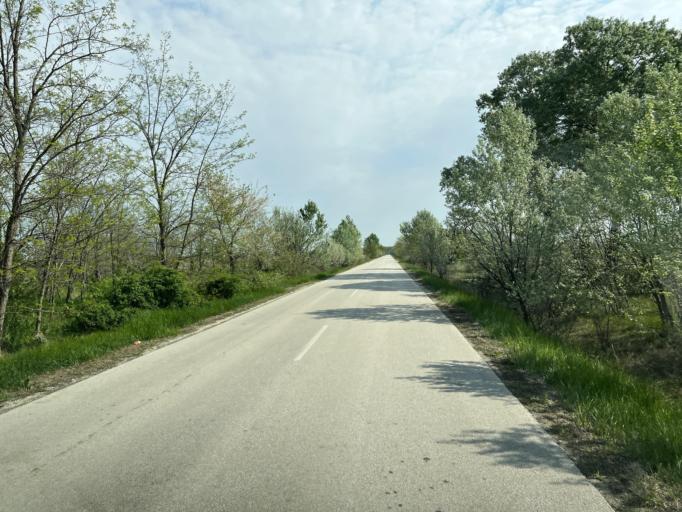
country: HU
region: Pest
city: Jaszkarajeno
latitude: 47.0767
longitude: 20.0059
